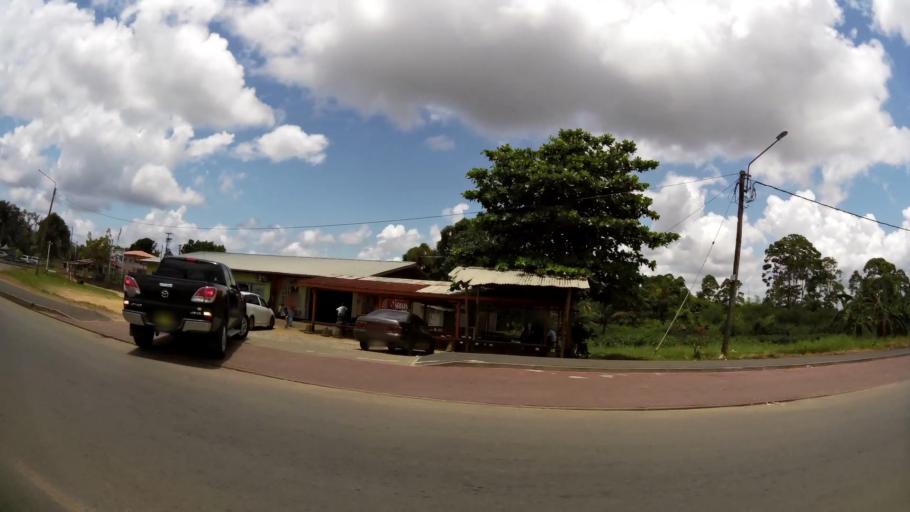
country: SR
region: Paramaribo
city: Paramaribo
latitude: 5.8013
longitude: -55.1230
